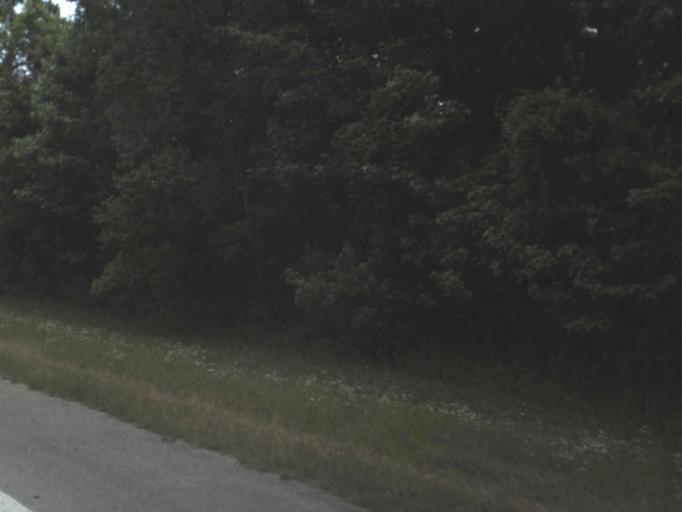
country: US
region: Florida
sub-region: Saint Johns County
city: Saint Augustine Shores
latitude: 29.7564
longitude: -81.3179
